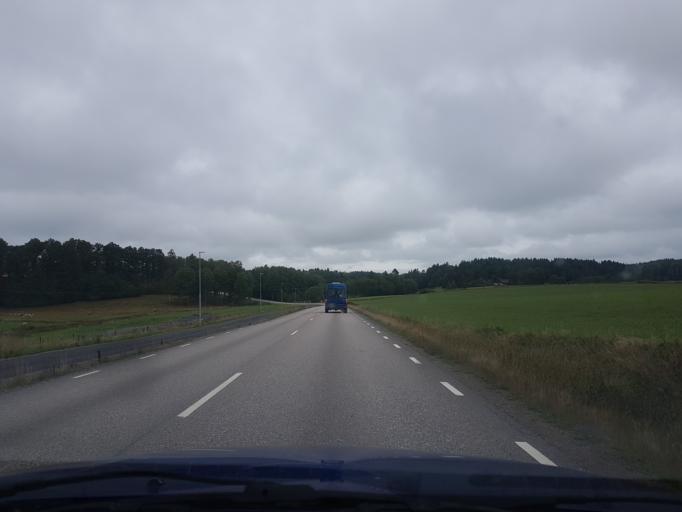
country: SE
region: Vaestra Goetaland
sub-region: Ale Kommun
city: Alvangen
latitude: 57.9438
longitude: 12.1406
